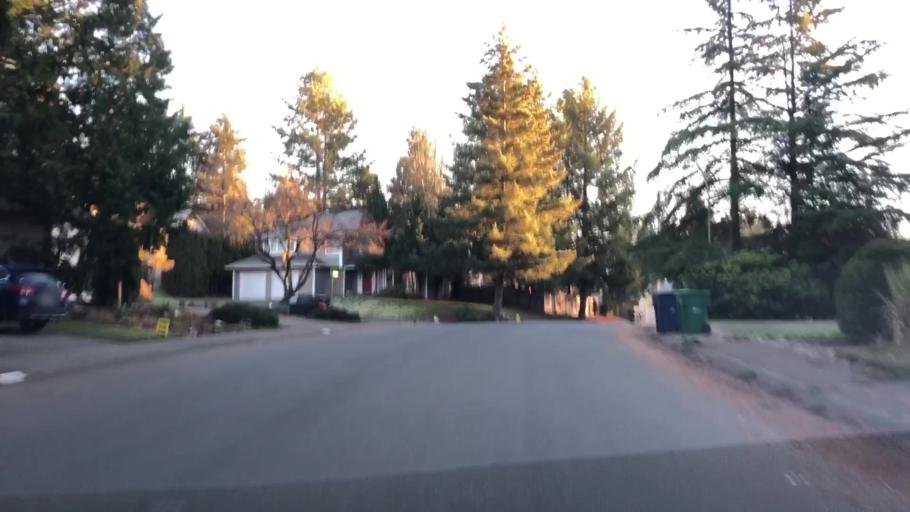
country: US
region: Washington
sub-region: King County
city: Cottage Lake
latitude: 47.7239
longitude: -122.1051
